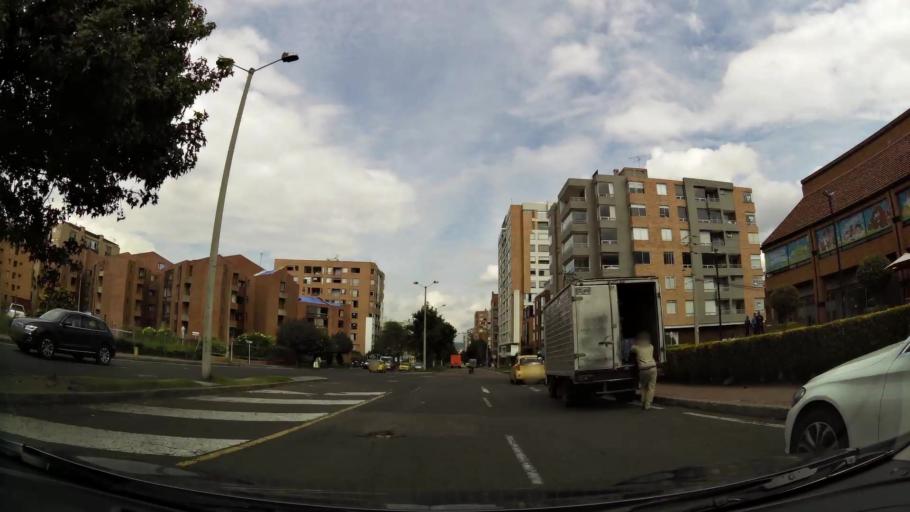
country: CO
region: Bogota D.C.
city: Barrio San Luis
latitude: 4.7233
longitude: -74.0274
